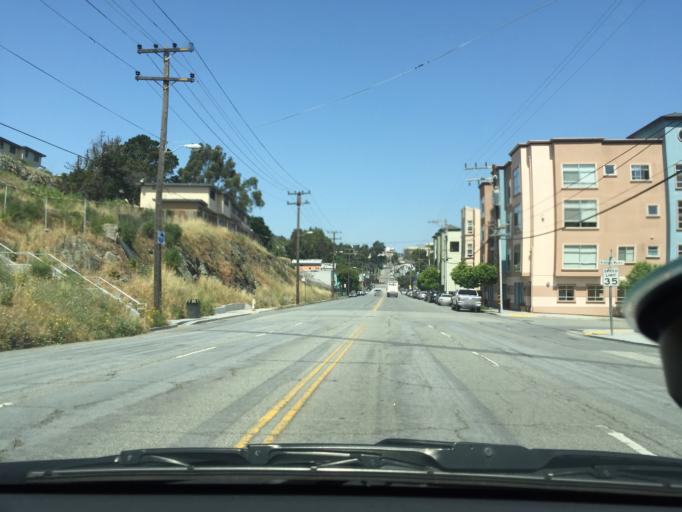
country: US
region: California
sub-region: San Mateo County
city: Brisbane
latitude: 37.7307
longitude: -122.3735
